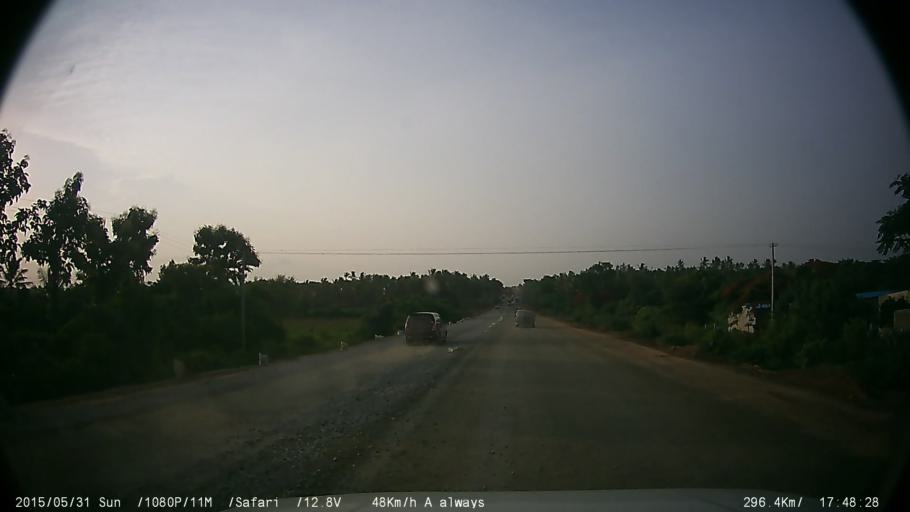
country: IN
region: Karnataka
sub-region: Mysore
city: Nanjangud
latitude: 11.9662
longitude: 76.6703
